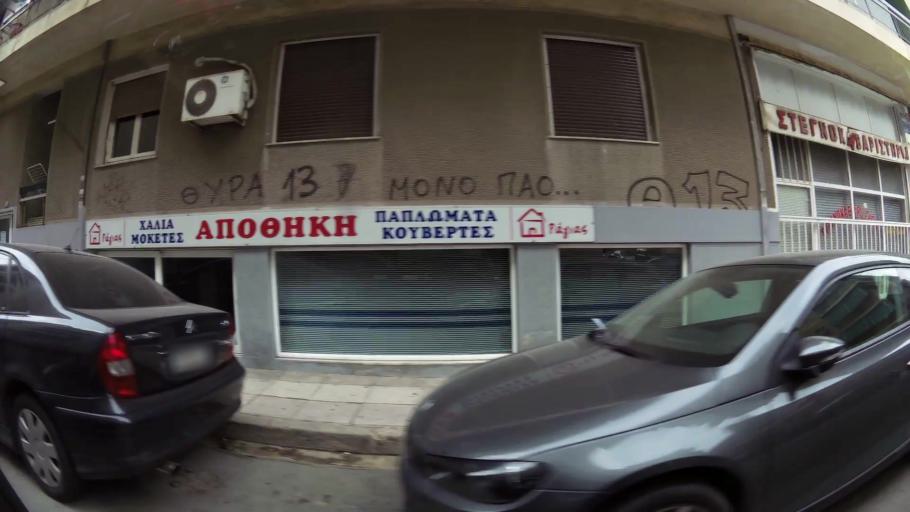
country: GR
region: Attica
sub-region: Nomarchia Athinas
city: Kipseli
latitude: 38.0093
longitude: 23.7255
